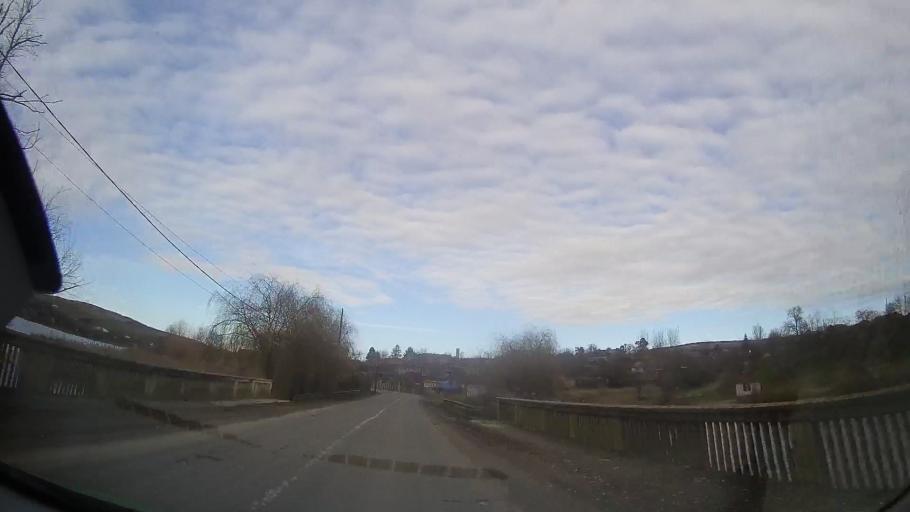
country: RO
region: Cluj
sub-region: Comuna Geaca
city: Geaca
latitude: 46.8521
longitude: 24.0916
